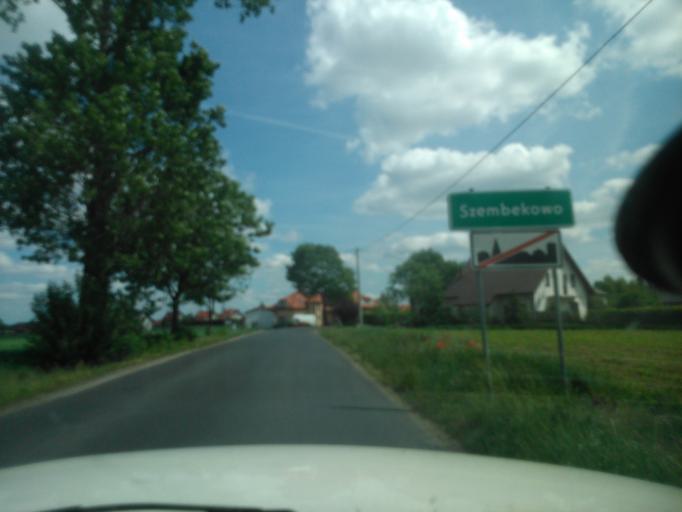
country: PL
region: Kujawsko-Pomorskie
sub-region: Powiat torunski
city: Lubicz Gorny
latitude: 53.0306
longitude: 18.8299
